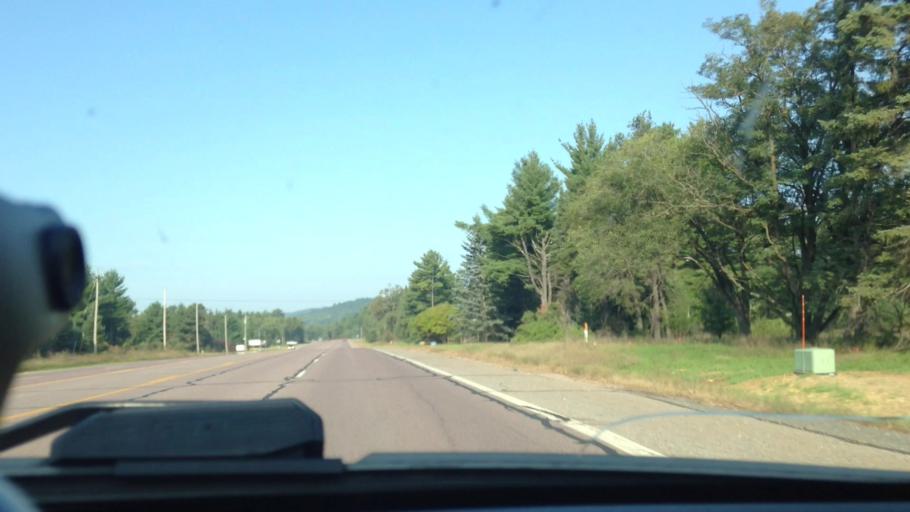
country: US
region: Michigan
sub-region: Dickinson County
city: Quinnesec
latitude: 45.8023
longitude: -87.9595
